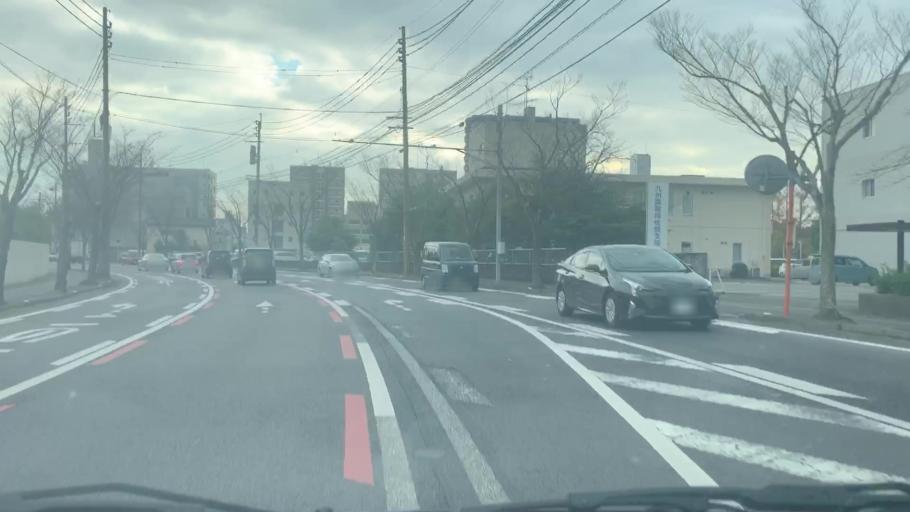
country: JP
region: Saga Prefecture
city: Saga-shi
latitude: 33.2644
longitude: 130.3021
